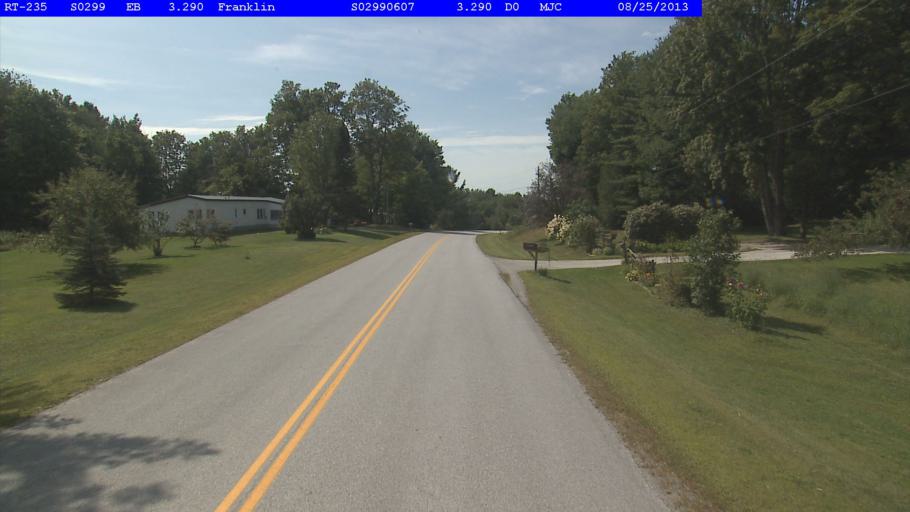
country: CA
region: Quebec
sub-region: Monteregie
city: Bedford
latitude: 45.0027
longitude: -72.9659
